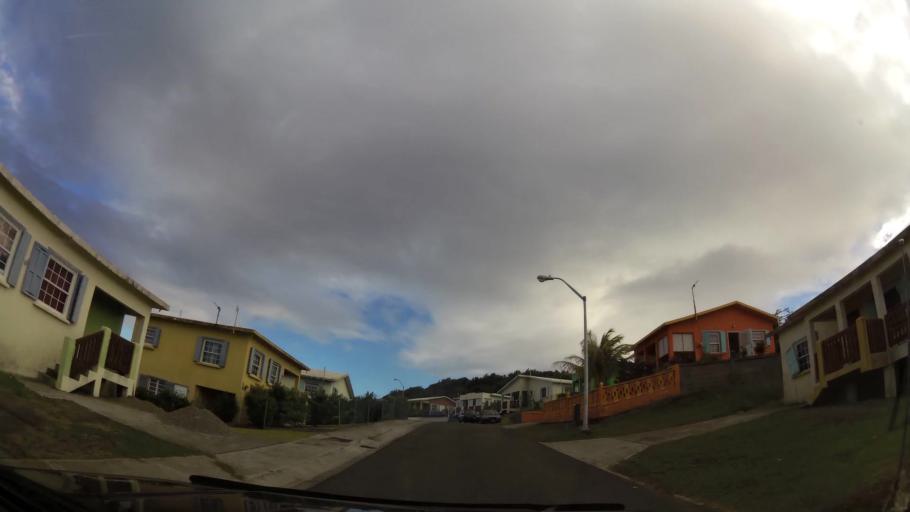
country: MS
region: Saint Peter
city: Brades
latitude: 16.7949
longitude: -62.1882
